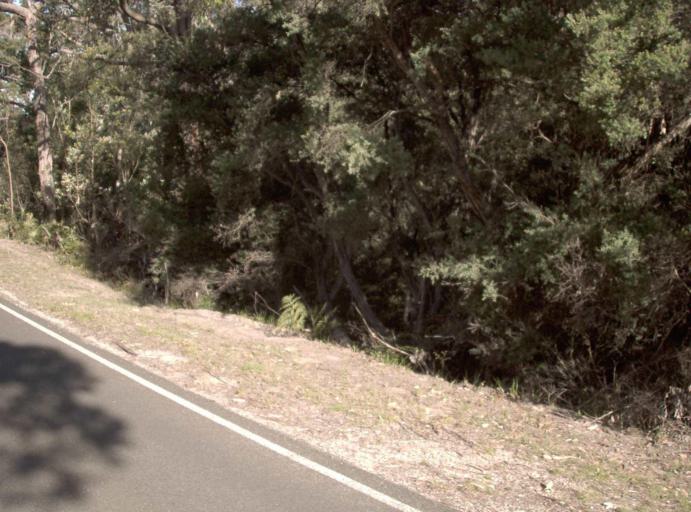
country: AU
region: Victoria
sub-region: East Gippsland
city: Lakes Entrance
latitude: -37.7995
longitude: 148.7353
